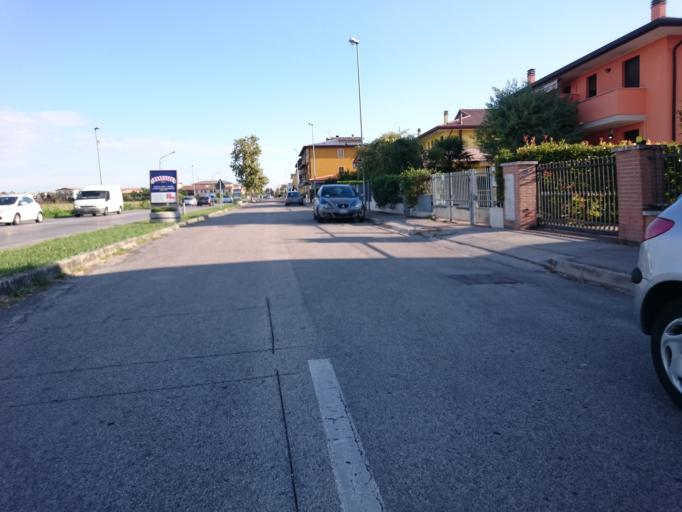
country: IT
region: Veneto
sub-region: Provincia di Padova
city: Masera di Padova
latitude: 45.3334
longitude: 11.8653
